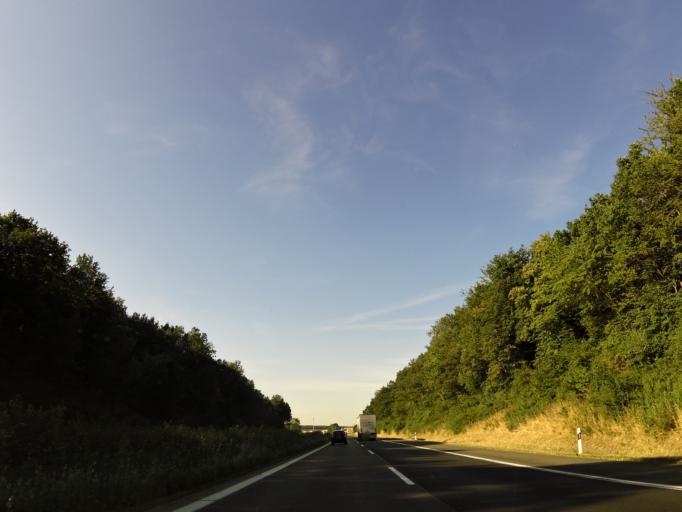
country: DE
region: Bavaria
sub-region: Regierungsbezirk Mittelfranken
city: Hessdorf
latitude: 49.5952
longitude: 10.9266
